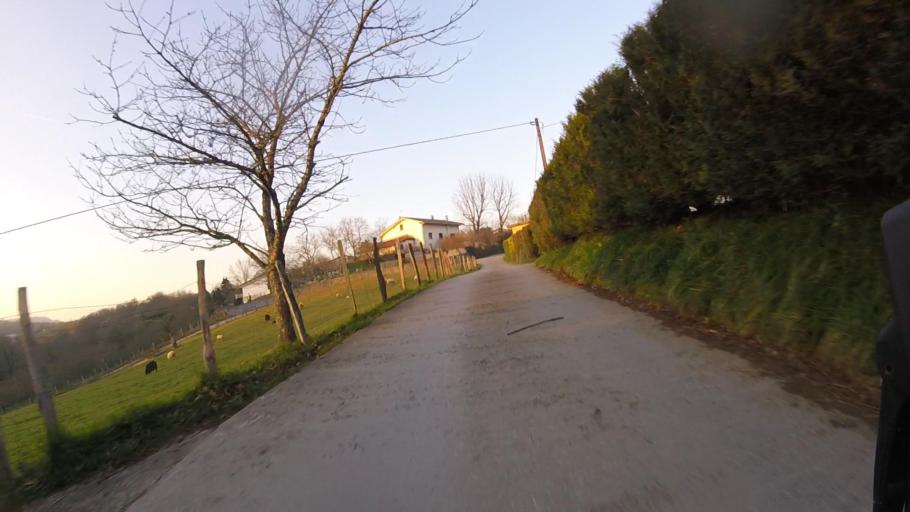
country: ES
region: Basque Country
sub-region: Provincia de Guipuzcoa
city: Errenteria
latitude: 43.2870
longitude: -1.8698
